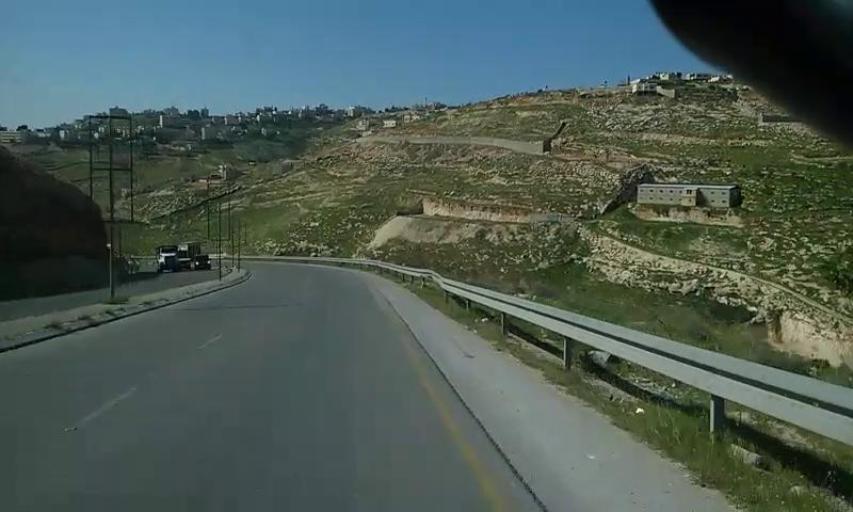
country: PS
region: West Bank
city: Abu Dis
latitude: 31.7497
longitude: 35.2780
